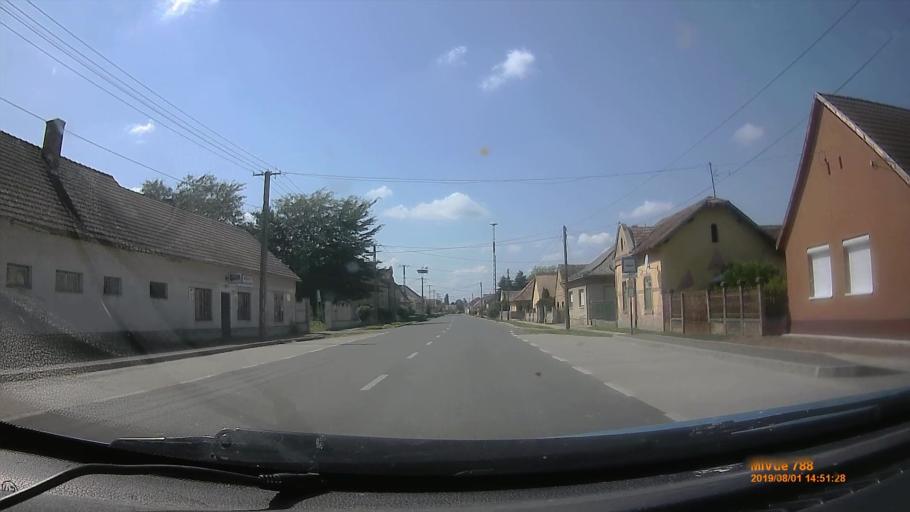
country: HU
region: Baranya
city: Vajszlo
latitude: 45.8556
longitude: 17.9946
